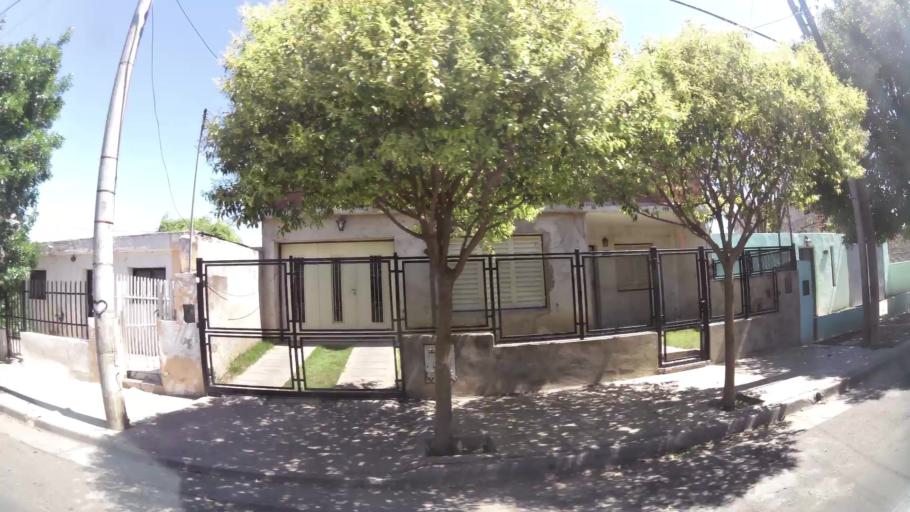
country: AR
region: Cordoba
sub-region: Departamento de Capital
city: Cordoba
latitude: -31.3784
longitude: -64.1615
